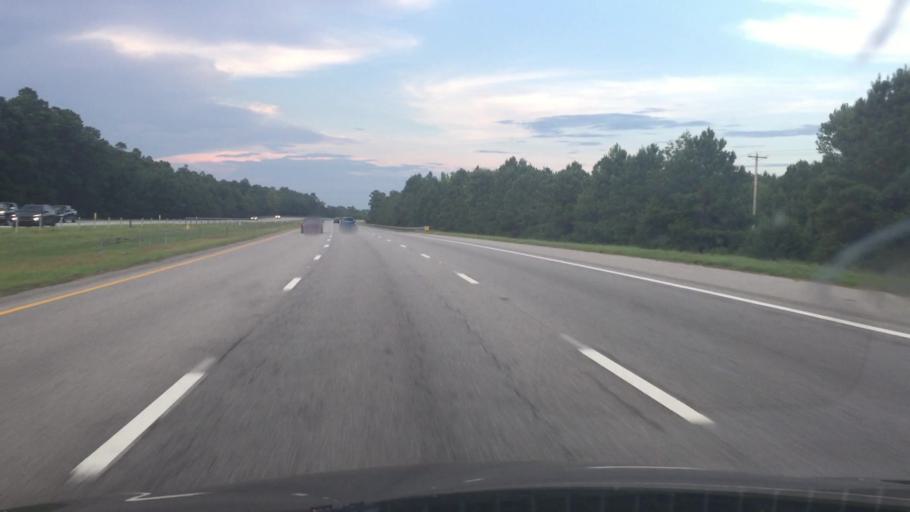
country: US
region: South Carolina
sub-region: Horry County
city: Myrtle Beach
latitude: 33.7618
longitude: -78.8379
